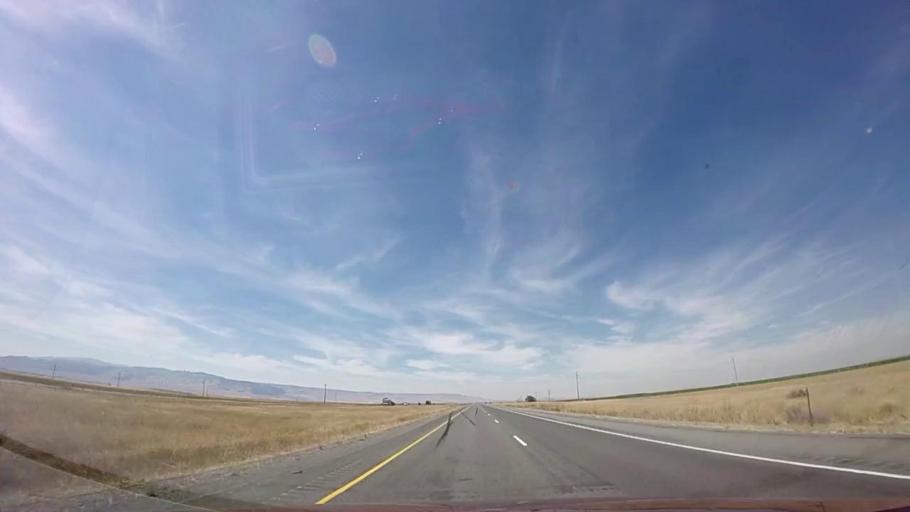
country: US
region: Idaho
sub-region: Minidoka County
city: Rupert
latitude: 42.3407
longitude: -113.2310
